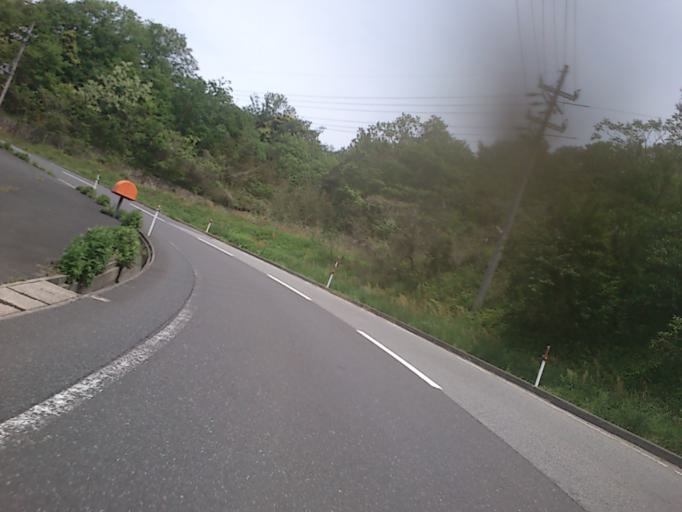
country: JP
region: Kyoto
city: Miyazu
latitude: 35.6939
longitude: 135.0506
